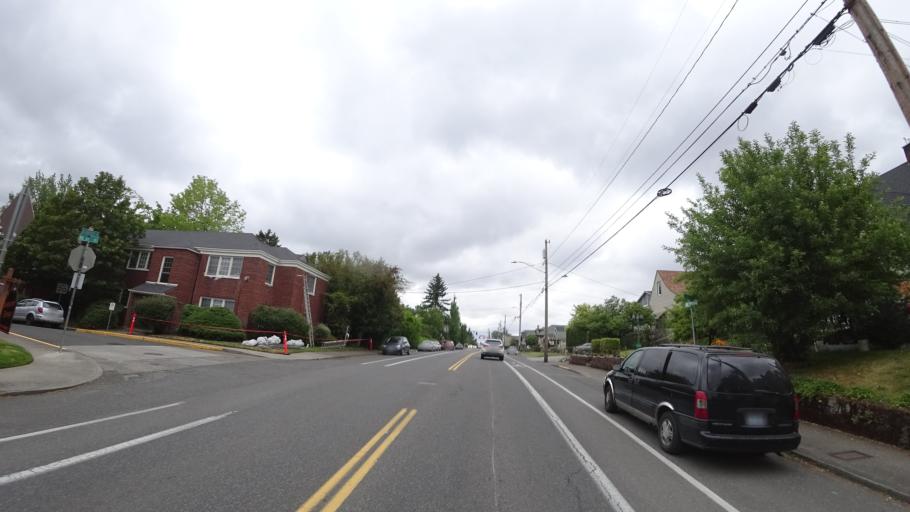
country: US
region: Oregon
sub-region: Multnomah County
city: Lents
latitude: 45.5405
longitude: -122.6046
